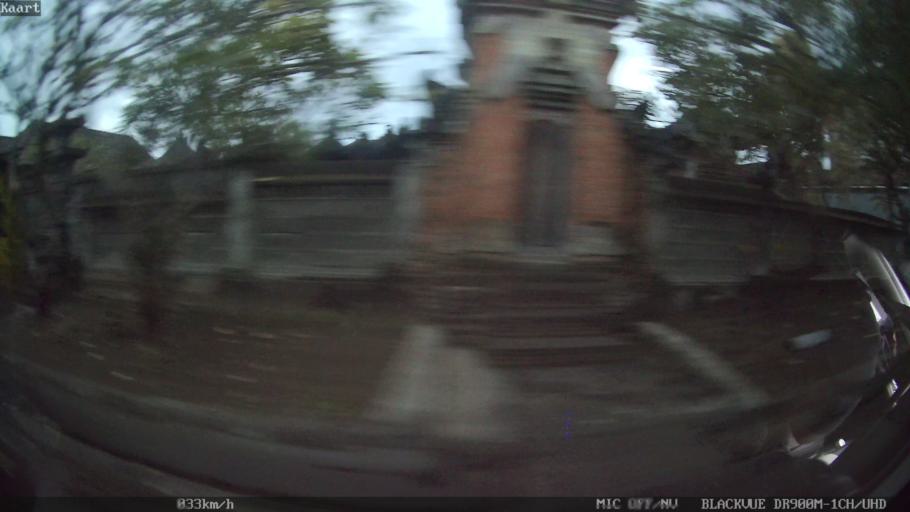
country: ID
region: Bali
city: Banjar Pasekan
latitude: -8.6199
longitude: 115.2742
